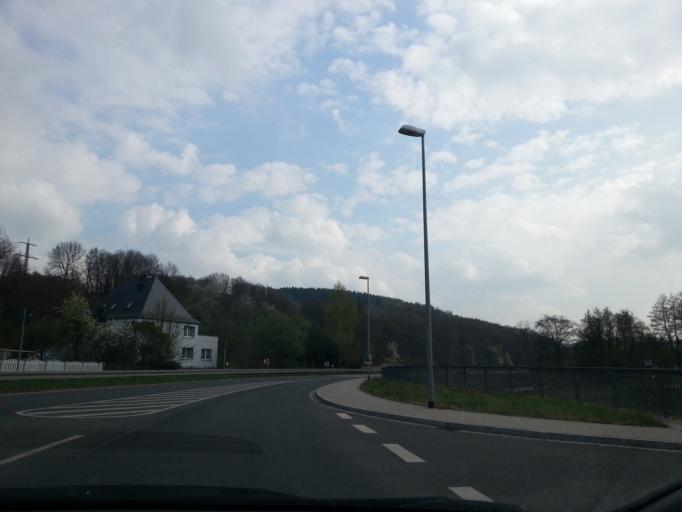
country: DE
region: Saxony
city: Dippoldiswalde
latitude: 50.8700
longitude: 13.6702
